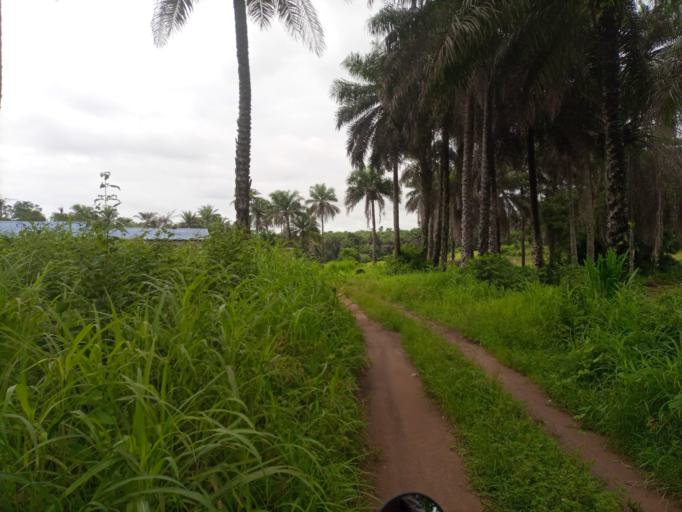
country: SL
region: Northern Province
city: Sawkta
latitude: 8.6448
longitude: -13.1895
